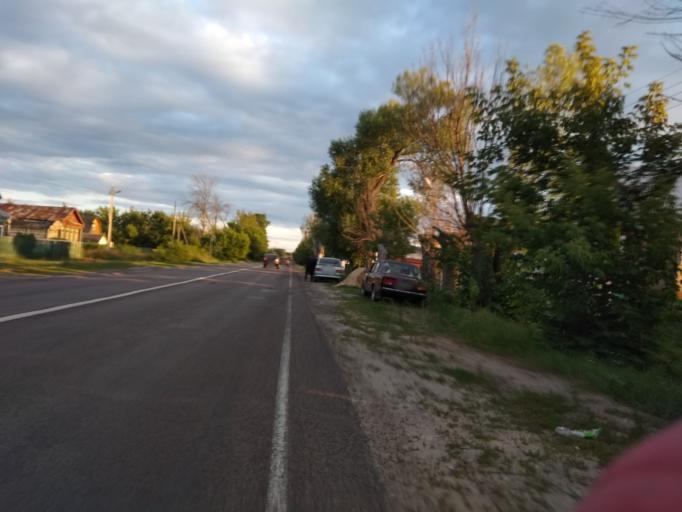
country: RU
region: Moskovskaya
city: Misheronskiy
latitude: 55.5967
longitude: 39.7033
